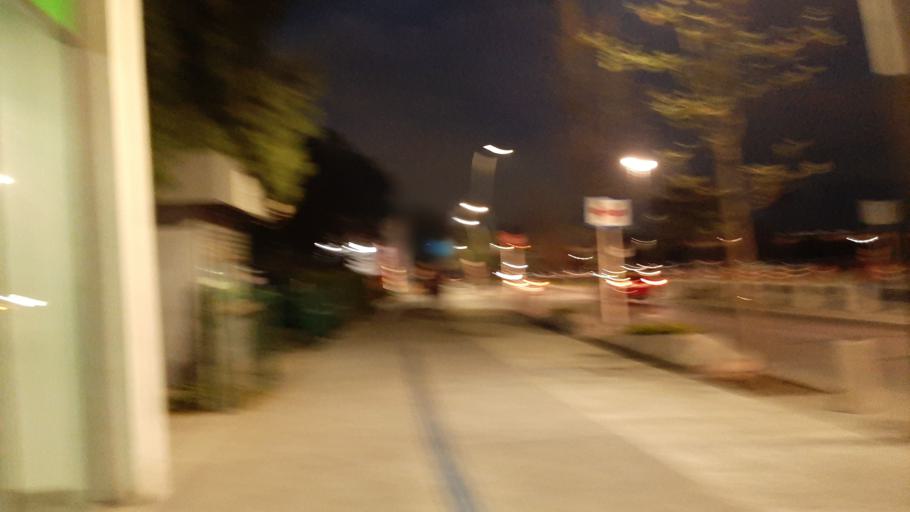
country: MX
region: Nuevo Leon
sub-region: San Nicolas de los Garza
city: San Nicolas de los Garza
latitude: 25.7238
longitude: -100.3115
